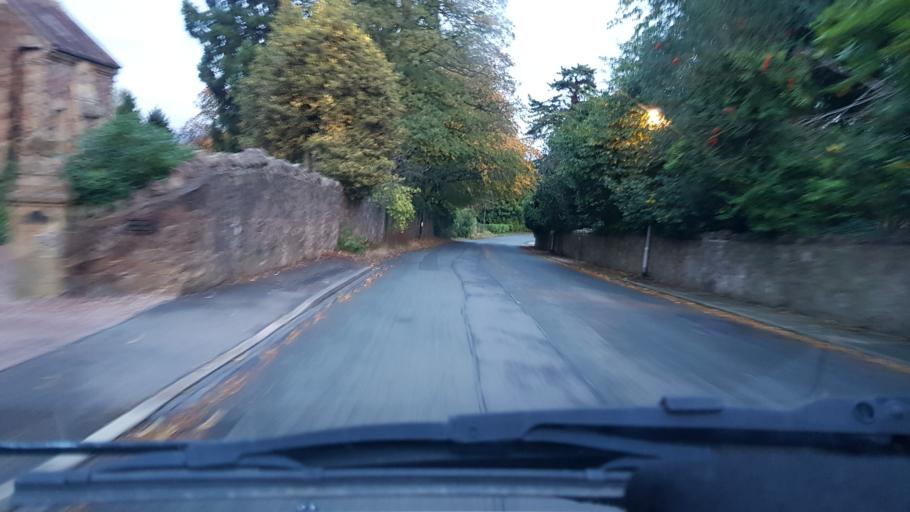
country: GB
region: England
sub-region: Worcestershire
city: Great Malvern
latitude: 52.1176
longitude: -2.3254
